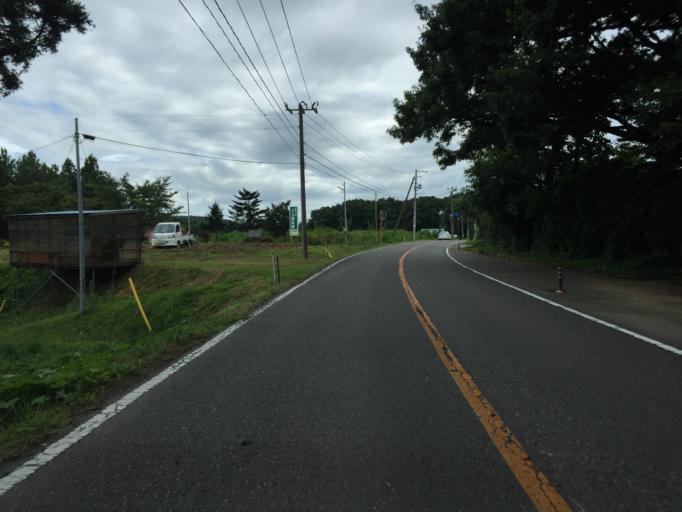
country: JP
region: Fukushima
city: Nihommatsu
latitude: 37.5813
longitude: 140.3528
